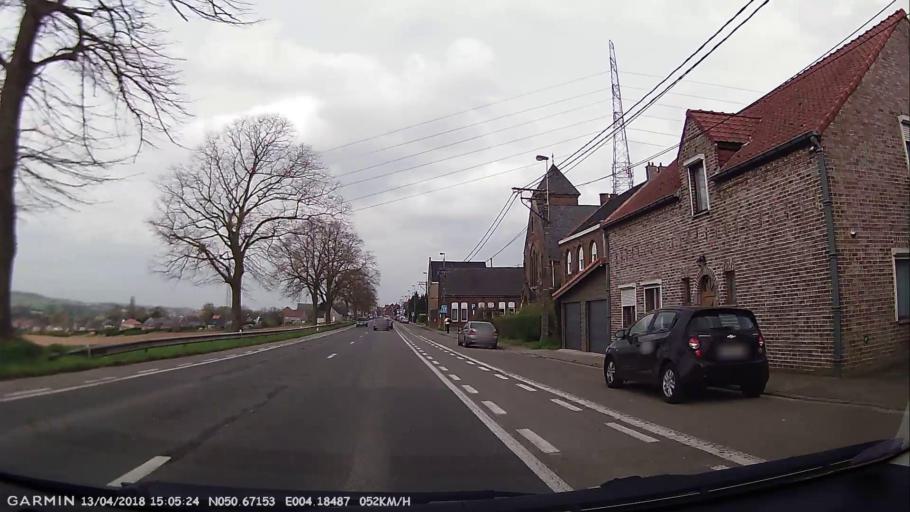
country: BE
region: Wallonia
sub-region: Province du Brabant Wallon
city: Tubize
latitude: 50.6717
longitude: 4.1850
